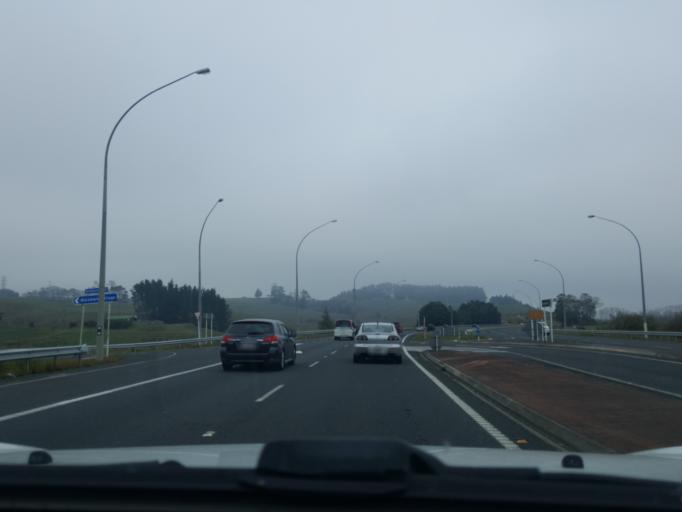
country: NZ
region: Waikato
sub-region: Waikato District
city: Te Kauwhata
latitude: -37.3252
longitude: 175.0663
